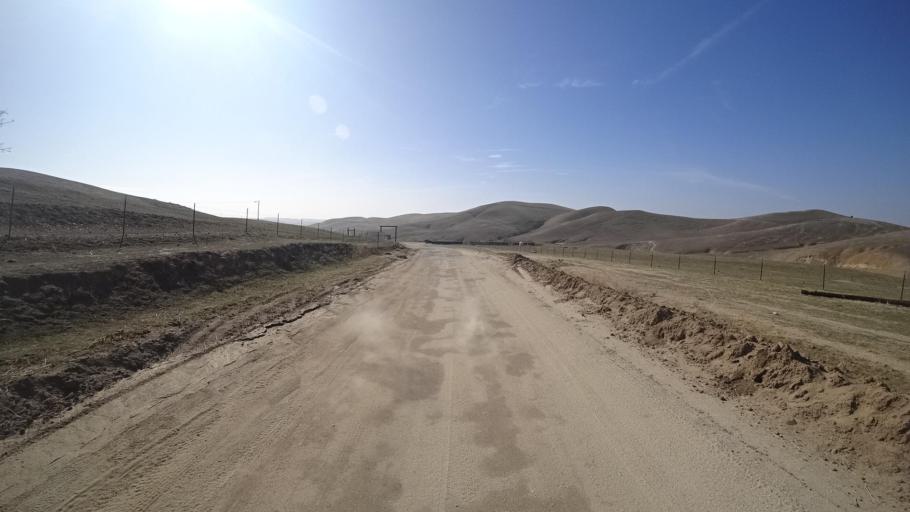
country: US
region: California
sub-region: Kern County
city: Oildale
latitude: 35.4724
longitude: -118.8286
